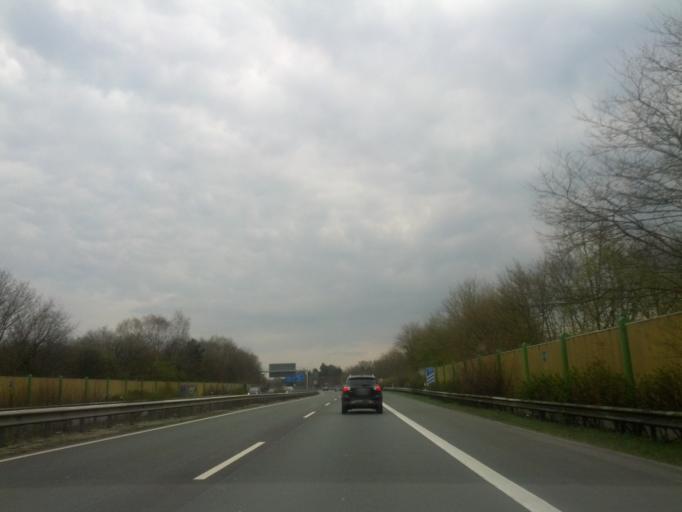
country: DE
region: Lower Saxony
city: Oldenburg
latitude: 53.1543
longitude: 8.1847
